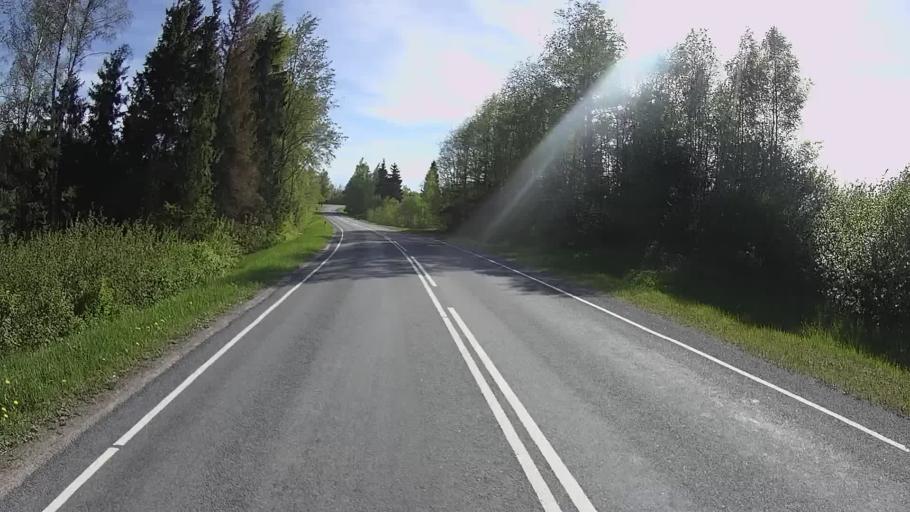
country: EE
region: Vorumaa
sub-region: Antsla vald
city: Vana-Antsla
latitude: 57.9617
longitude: 26.4539
